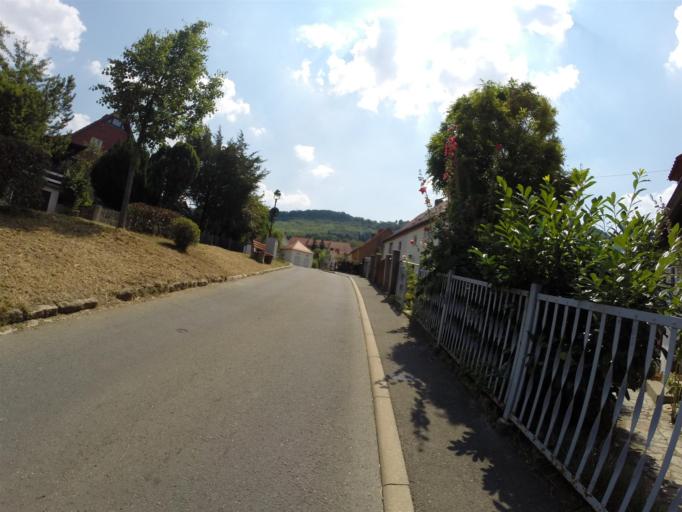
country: DE
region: Thuringia
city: Jena
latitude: 50.9301
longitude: 11.6207
